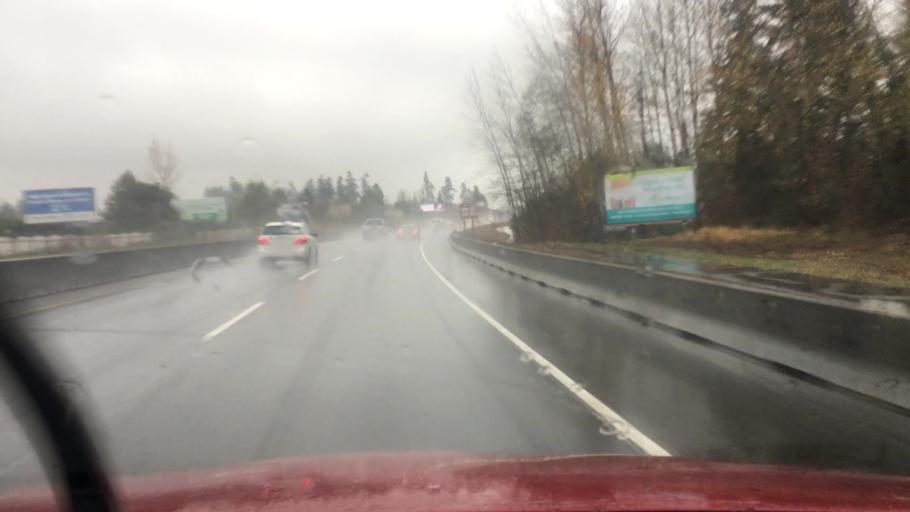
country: CA
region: British Columbia
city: North Saanich
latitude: 48.5872
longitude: -123.4012
